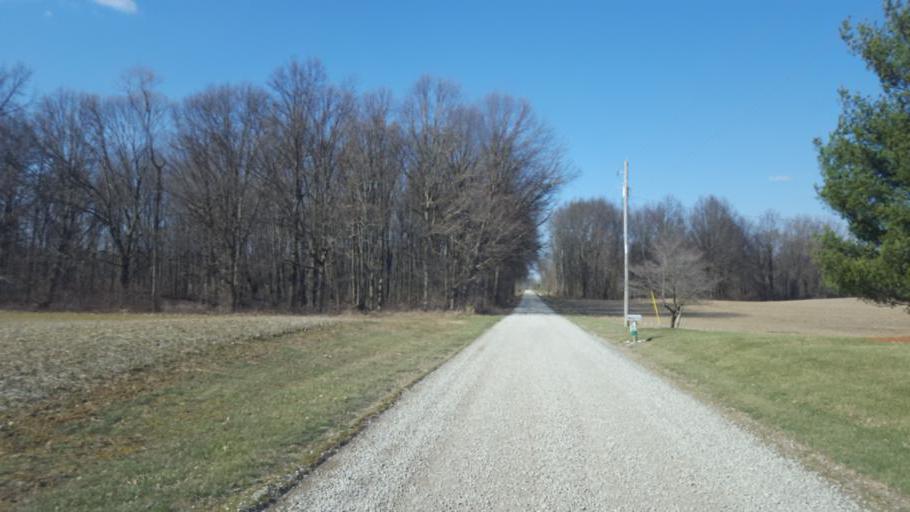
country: US
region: Ohio
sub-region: Morrow County
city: Mount Gilead
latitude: 40.5255
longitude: -82.7781
